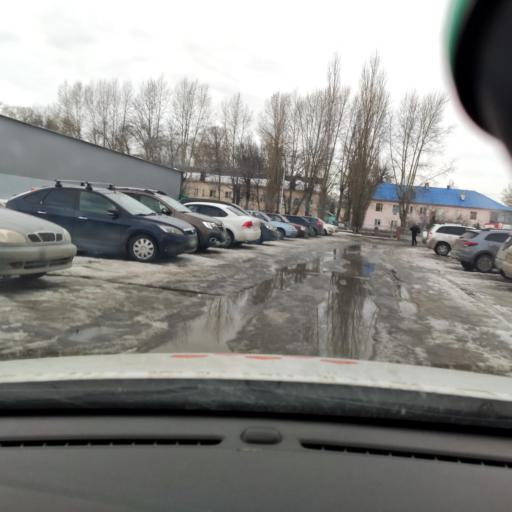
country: RU
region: Bashkortostan
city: Mikhaylovka
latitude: 54.6975
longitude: 55.8346
